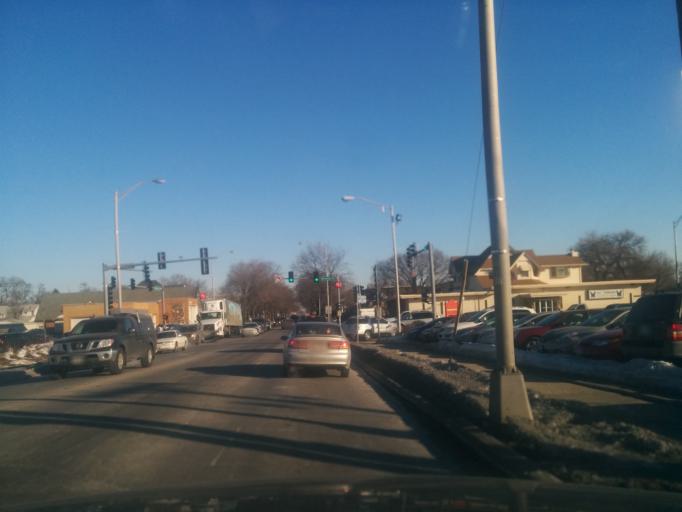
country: US
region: Illinois
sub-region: Cook County
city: Franklin Park
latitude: 41.9363
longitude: -87.8654
